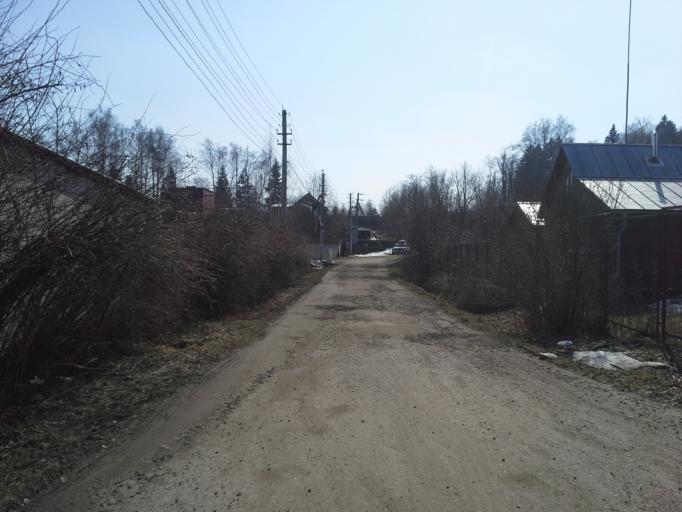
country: RU
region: Moskovskaya
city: Filimonki
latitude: 55.5450
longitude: 37.3854
